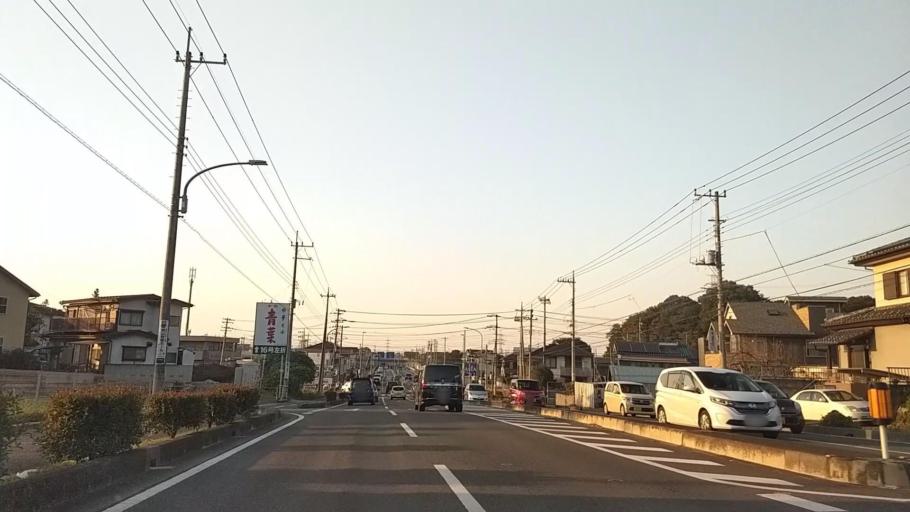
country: JP
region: Saitama
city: Sayama
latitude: 35.8635
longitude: 139.4271
